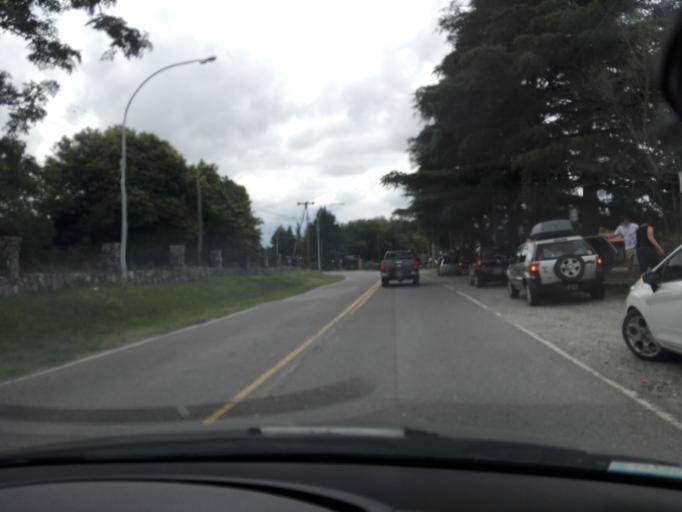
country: AR
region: Cordoba
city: Alta Gracia
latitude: -31.5874
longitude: -64.4595
